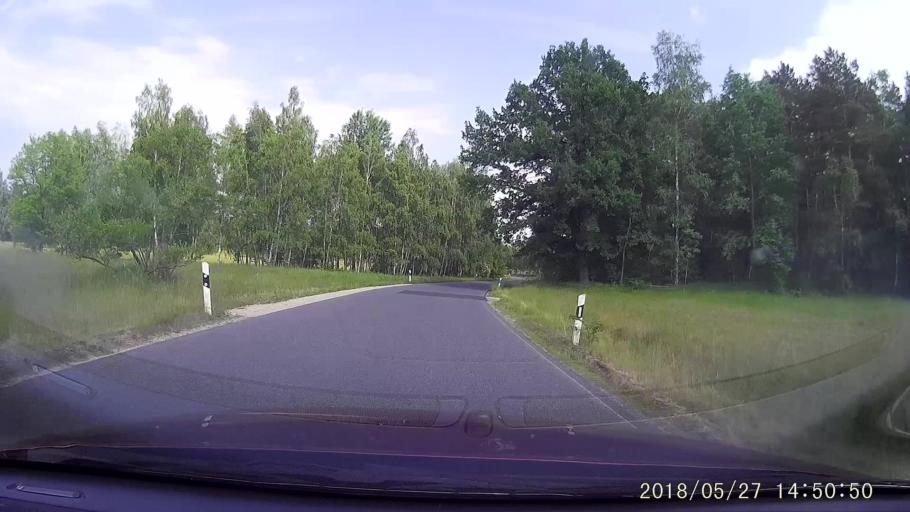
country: DE
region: Saxony
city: Klitten
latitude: 51.3567
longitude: 14.5623
